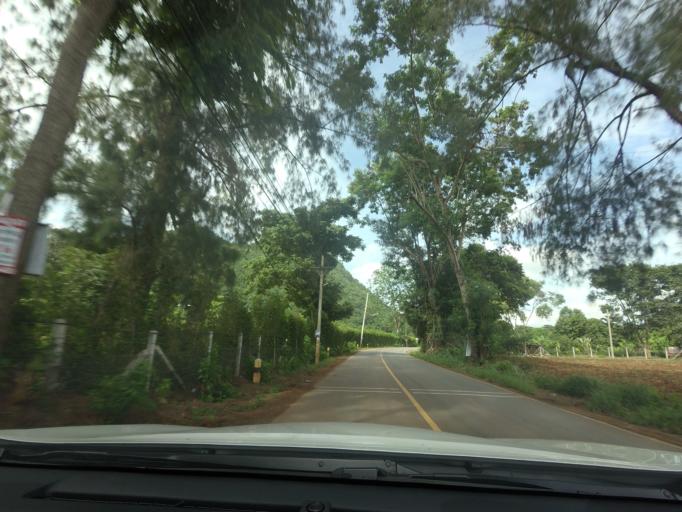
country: TH
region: Nakhon Ratchasima
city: Pak Chong
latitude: 14.5461
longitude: 101.4147
